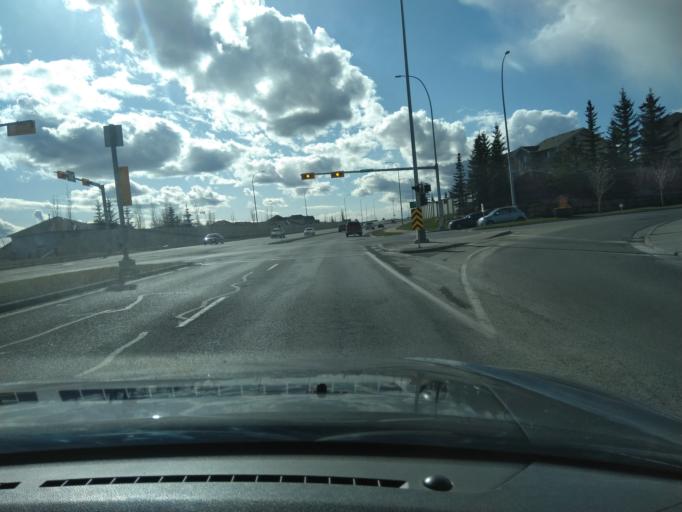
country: CA
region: Alberta
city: Calgary
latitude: 51.1428
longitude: -114.1949
